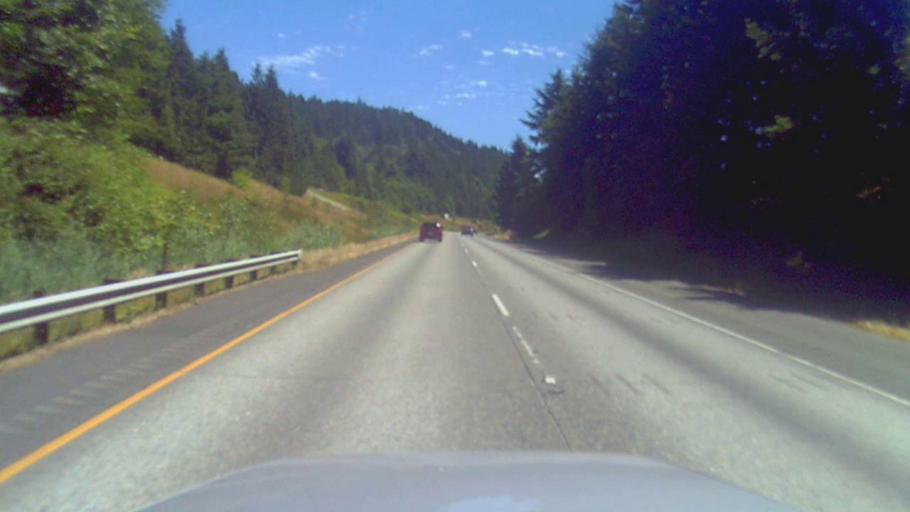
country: US
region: Washington
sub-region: Whatcom County
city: Bellingham
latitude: 48.6980
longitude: -122.4617
